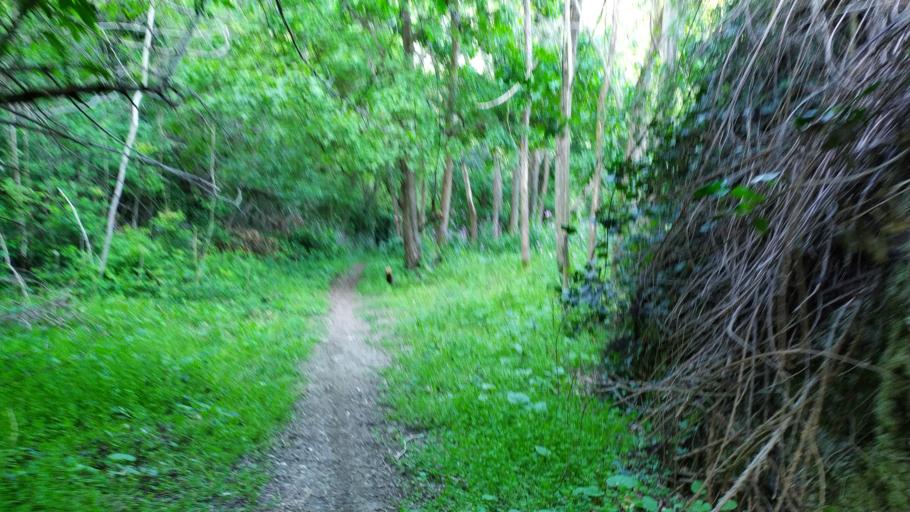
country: IT
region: Emilia-Romagna
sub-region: Provincia di Bologna
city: Borgo Tossignano
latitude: 44.2712
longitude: 11.6057
